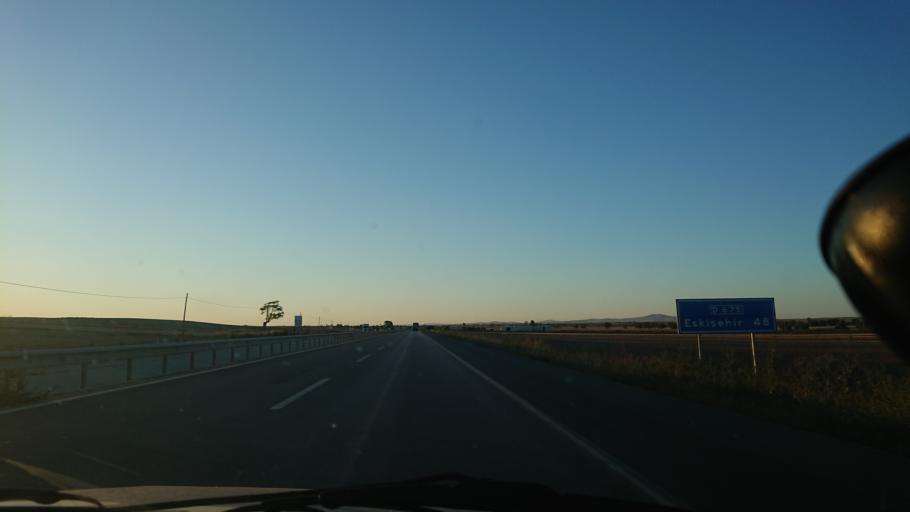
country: TR
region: Eskisehir
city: Mahmudiye
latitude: 39.5220
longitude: 30.9587
